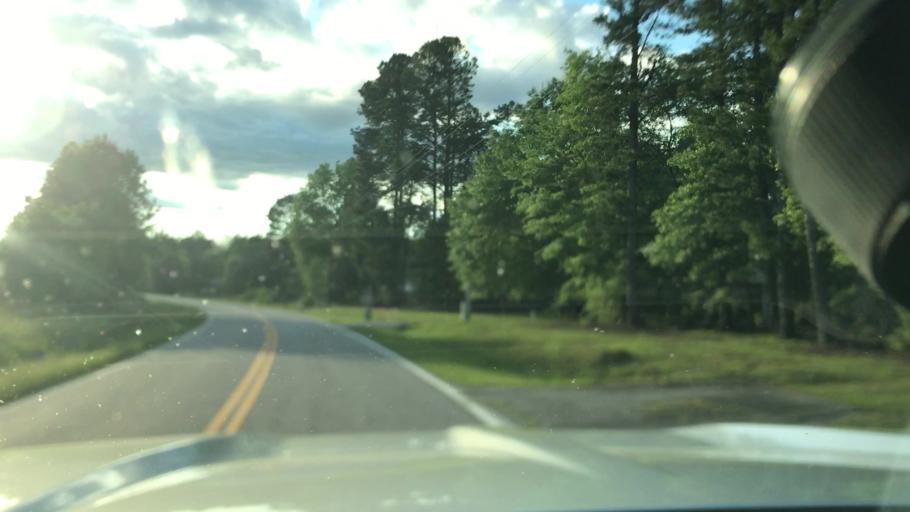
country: US
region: South Carolina
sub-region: Barnwell County
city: Blackville
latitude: 33.4737
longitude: -81.1743
